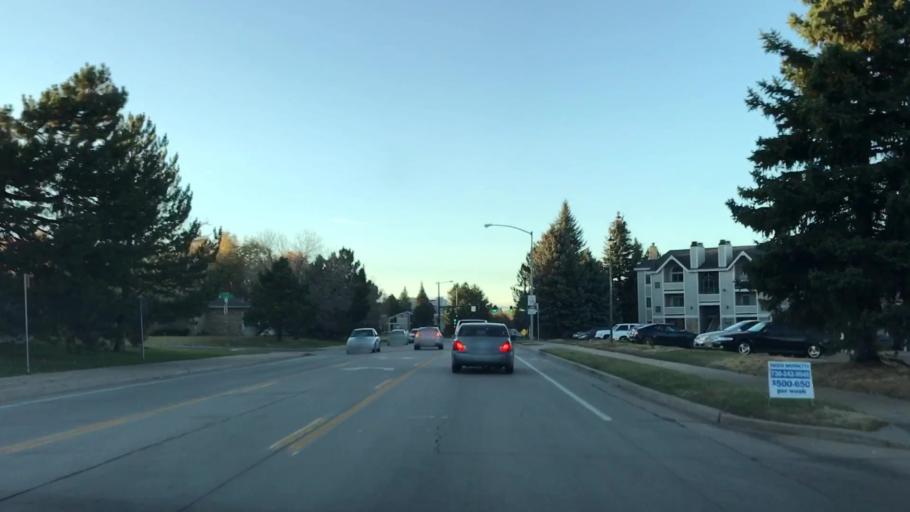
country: US
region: Colorado
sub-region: Arapahoe County
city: Glendale
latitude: 39.6665
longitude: -104.8928
